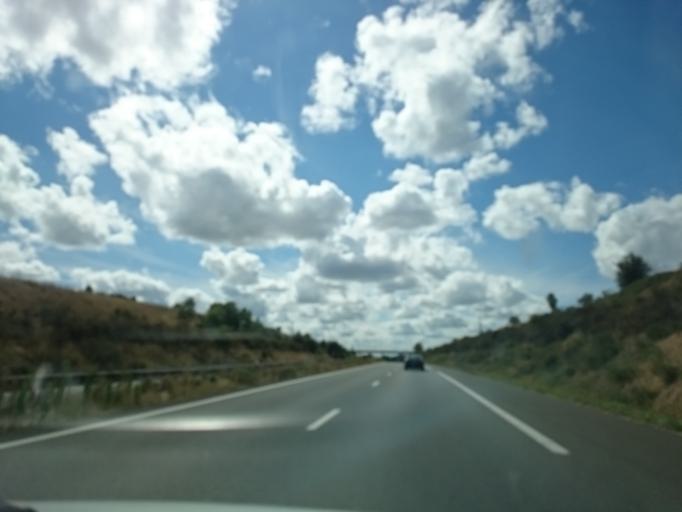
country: FR
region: Pays de la Loire
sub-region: Departement de Maine-et-Loire
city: Champtoce-sur-Loire
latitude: 47.4328
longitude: -0.8737
